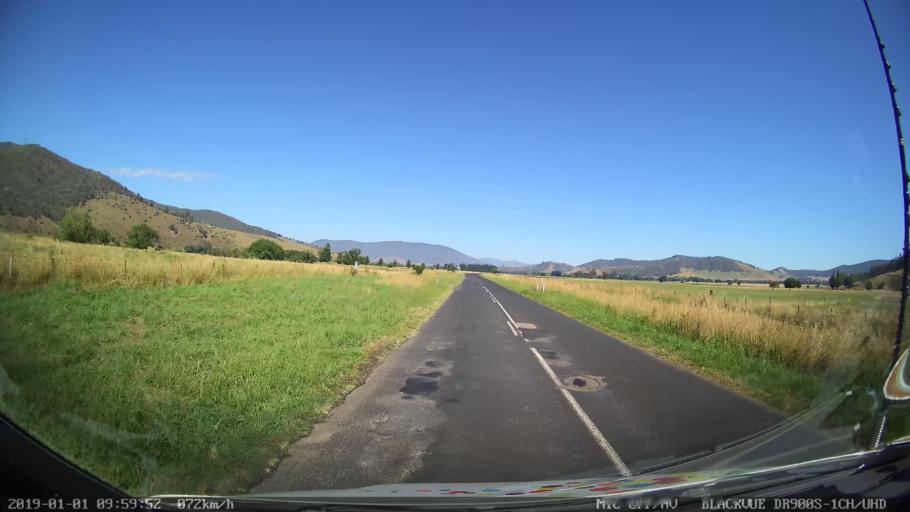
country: AU
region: New South Wales
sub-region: Snowy River
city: Jindabyne
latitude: -36.2068
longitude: 148.1039
